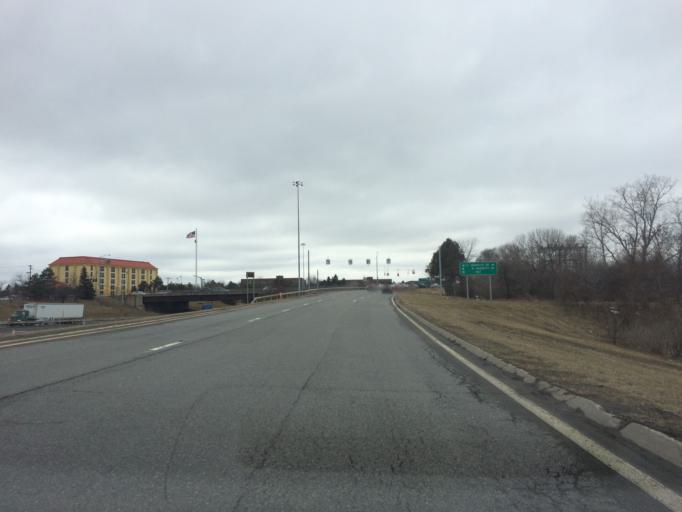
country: US
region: New York
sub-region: Monroe County
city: Rochester
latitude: 43.1082
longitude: -77.6134
